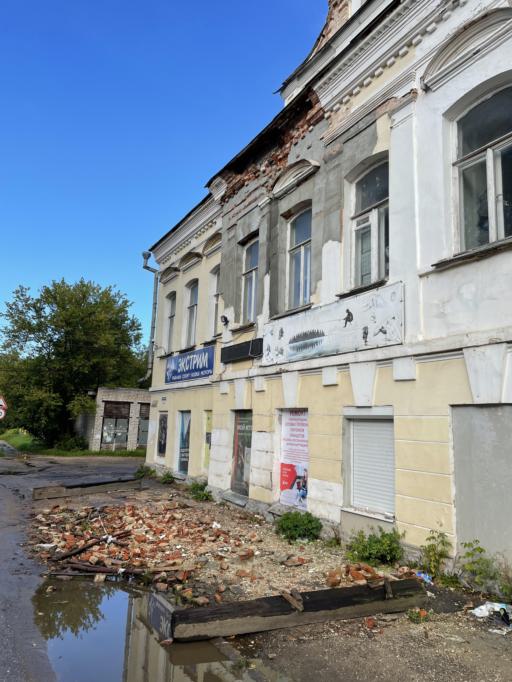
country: RU
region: Tverskaya
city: Vyshniy Volochek
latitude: 57.5844
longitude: 34.5498
